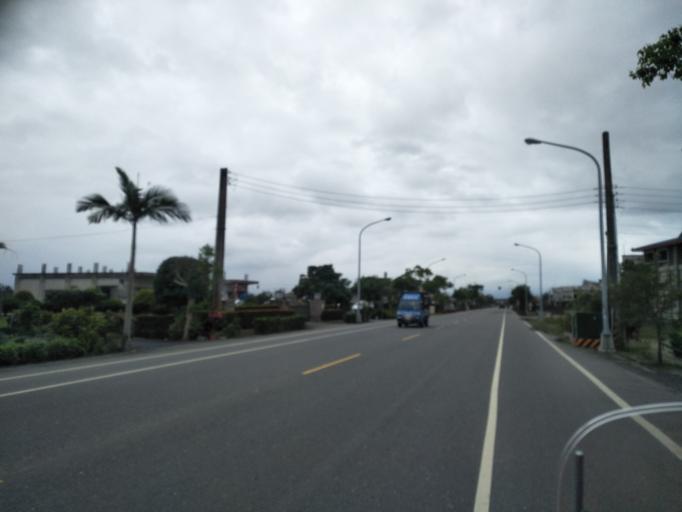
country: TW
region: Taiwan
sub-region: Yilan
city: Yilan
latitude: 24.7970
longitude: 121.7863
